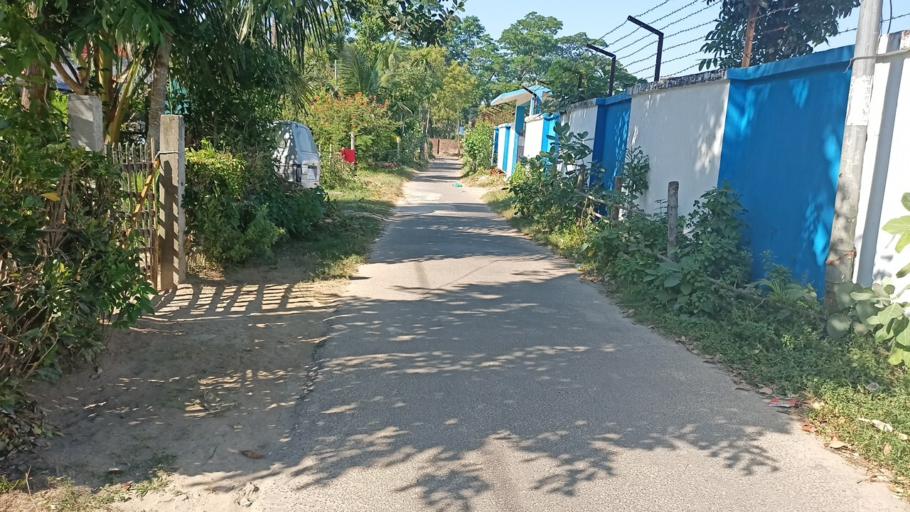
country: IN
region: West Bengal
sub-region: North 24 Parganas
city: Bangaon
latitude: 23.0523
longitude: 88.8256
